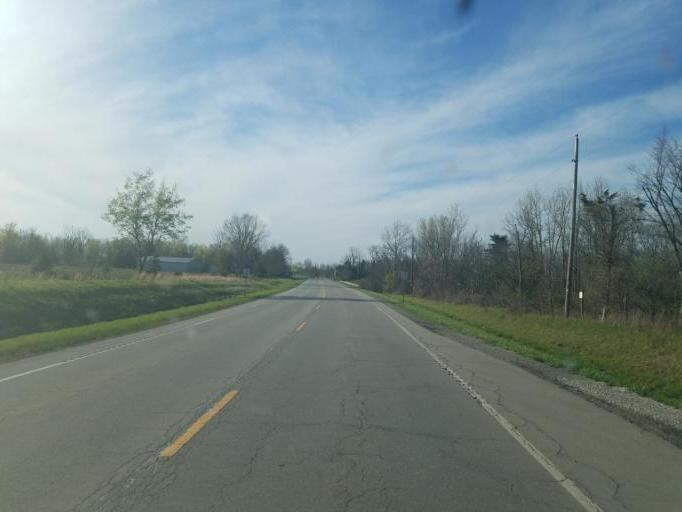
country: US
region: Ohio
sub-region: Huron County
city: New London
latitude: 41.0328
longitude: -82.4199
